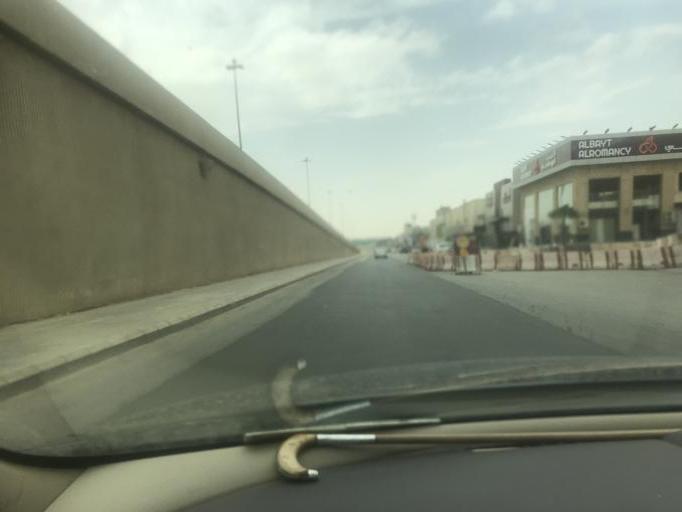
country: SA
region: Ar Riyad
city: Riyadh
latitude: 24.7915
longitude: 46.7014
